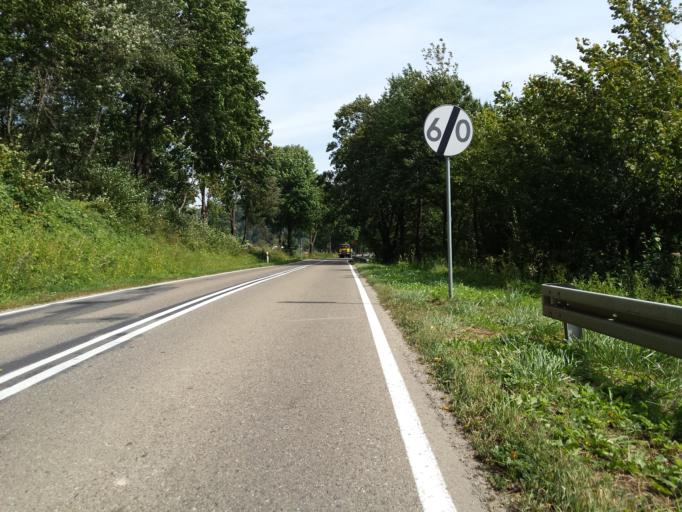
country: PL
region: Subcarpathian Voivodeship
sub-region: Powiat leski
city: Baligrod
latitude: 49.3839
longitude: 22.2832
